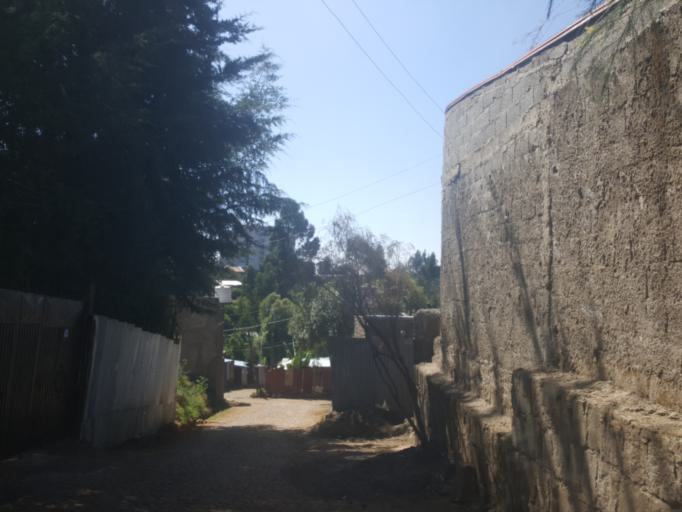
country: ET
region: Adis Abeba
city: Addis Ababa
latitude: 9.0711
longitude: 38.7340
